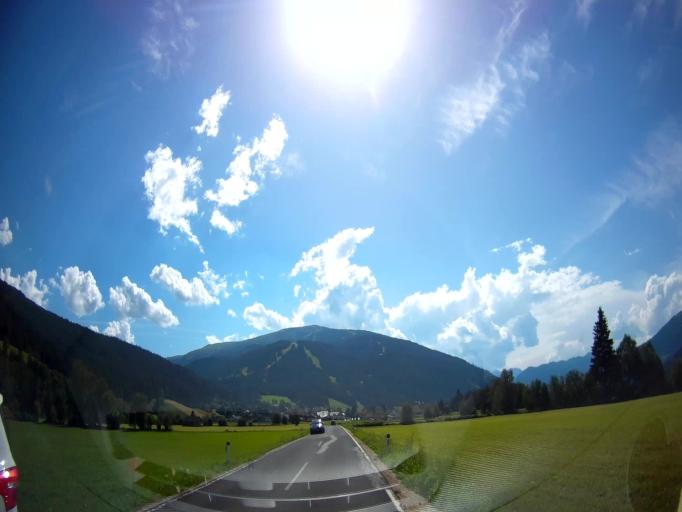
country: AT
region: Salzburg
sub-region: Politischer Bezirk Tamsweg
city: Sankt Margarethen im Lungau
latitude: 47.0849
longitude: 13.7081
